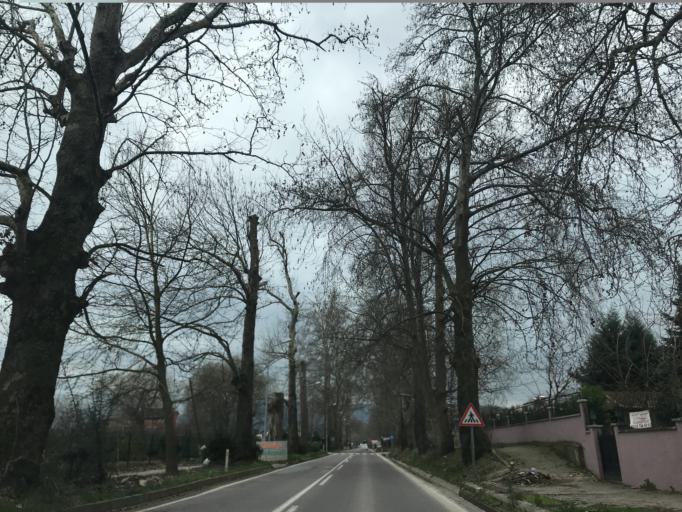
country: TR
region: Yalova
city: Kadikoy
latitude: 40.6418
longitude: 29.2288
